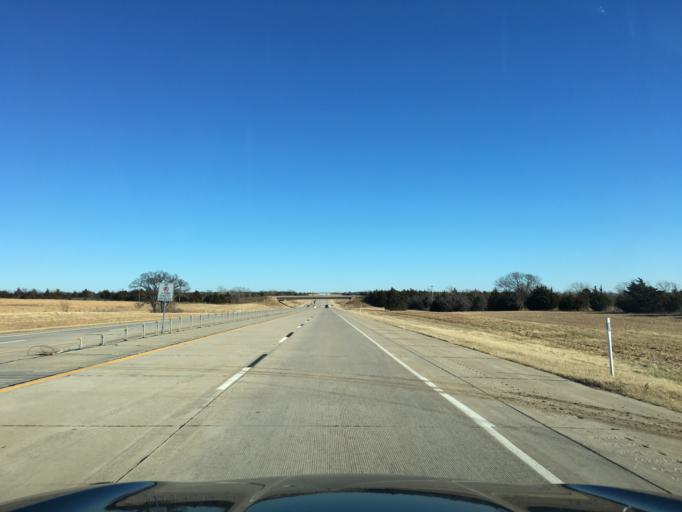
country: US
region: Oklahoma
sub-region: Payne County
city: Yale
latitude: 36.2250
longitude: -96.6822
